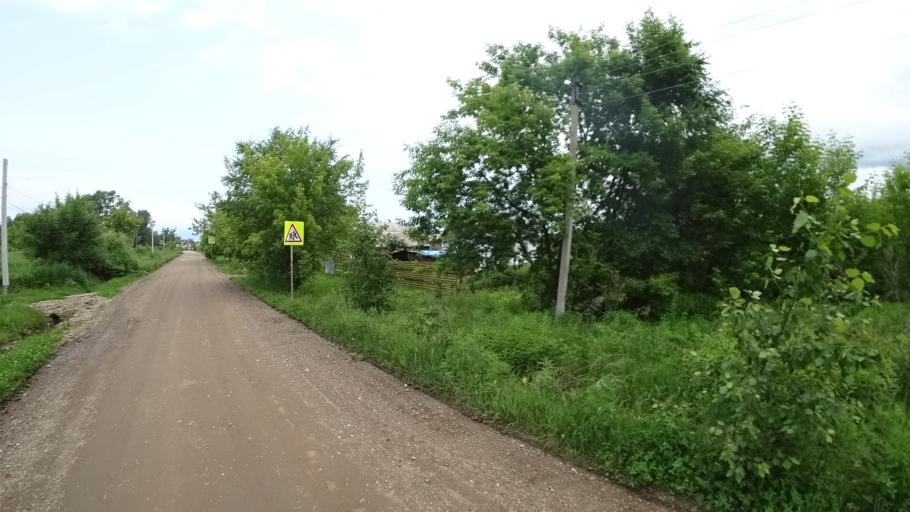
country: RU
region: Primorskiy
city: Novosysoyevka
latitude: 44.2372
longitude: 133.3648
